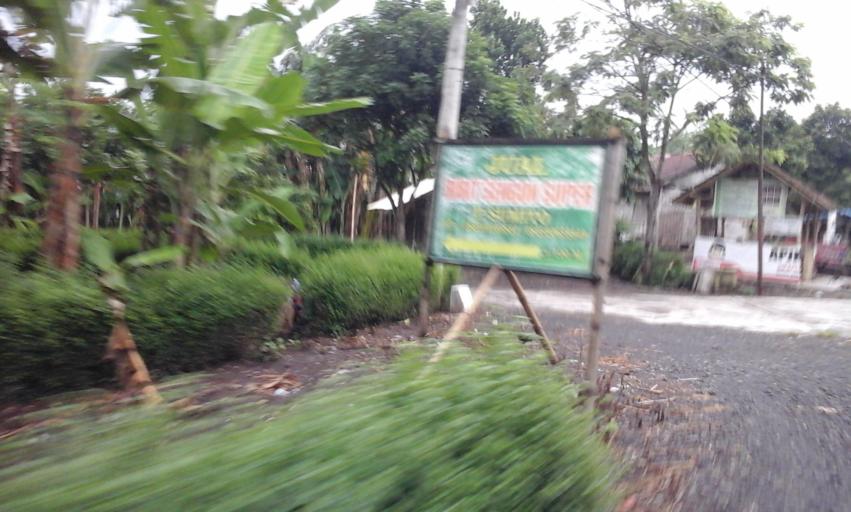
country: ID
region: East Java
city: Pondoktelo
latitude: -8.0988
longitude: 113.2677
